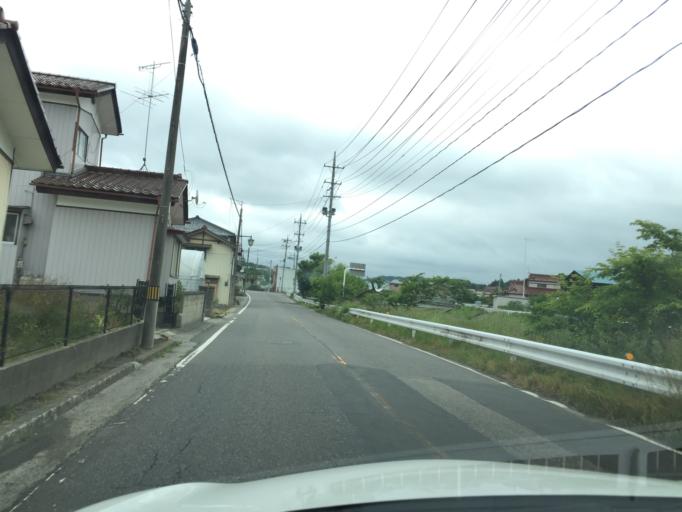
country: JP
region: Fukushima
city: Funehikimachi-funehiki
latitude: 37.4230
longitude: 140.6038
